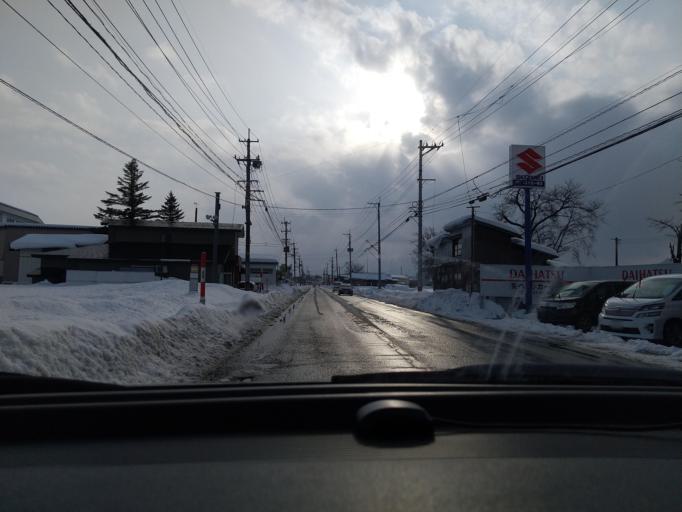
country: JP
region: Akita
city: Omagari
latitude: 39.4945
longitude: 140.4998
